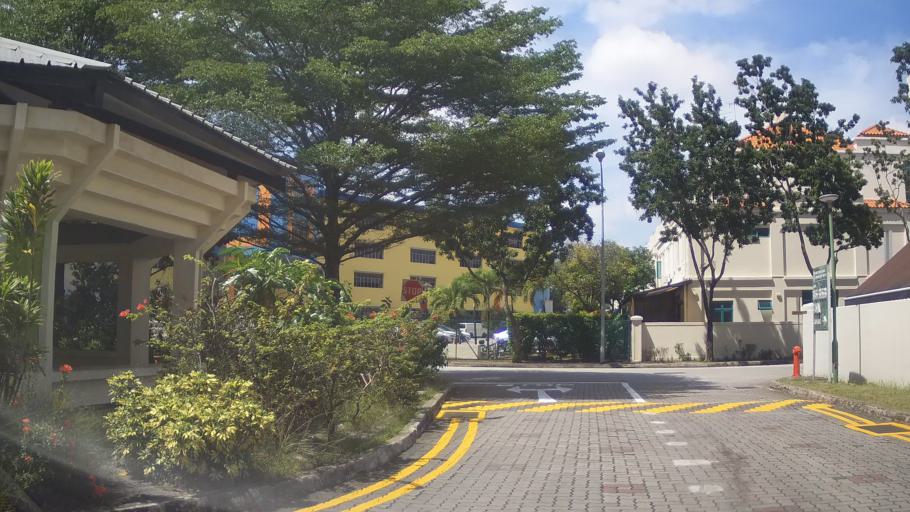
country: MY
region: Johor
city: Johor Bahru
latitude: 1.3393
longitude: 103.7188
